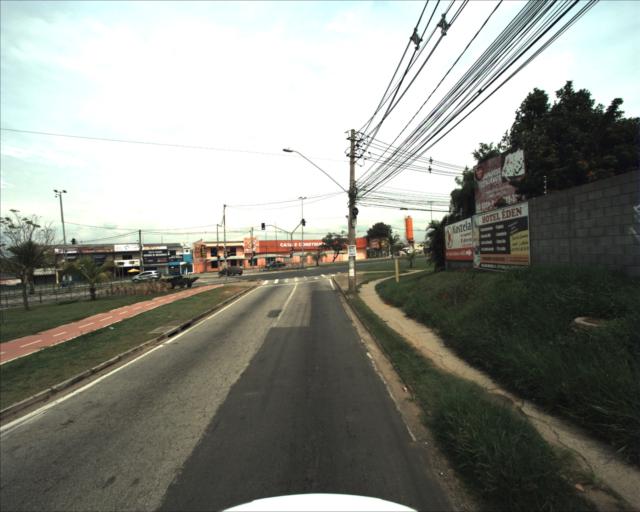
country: BR
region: Sao Paulo
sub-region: Sorocaba
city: Sorocaba
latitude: -23.4249
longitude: -47.4142
